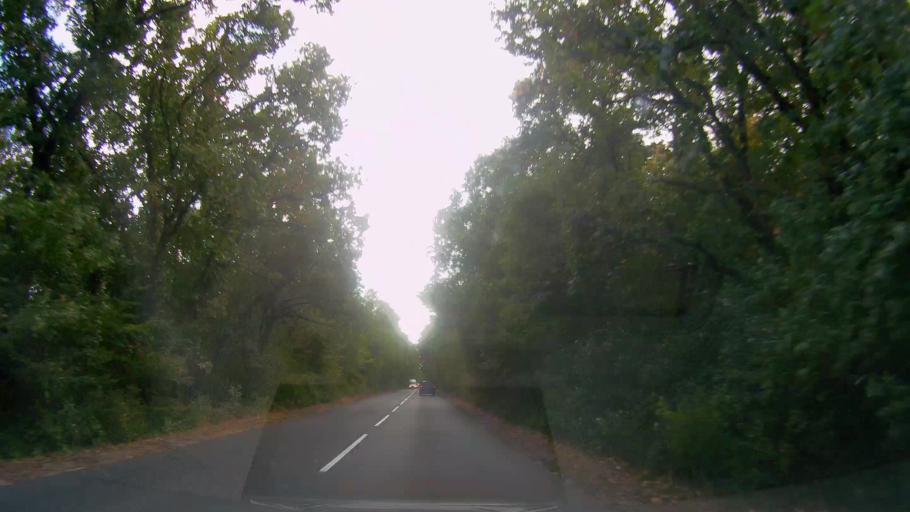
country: BG
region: Burgas
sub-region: Obshtina Primorsko
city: Primorsko
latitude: 42.2996
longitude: 27.7294
